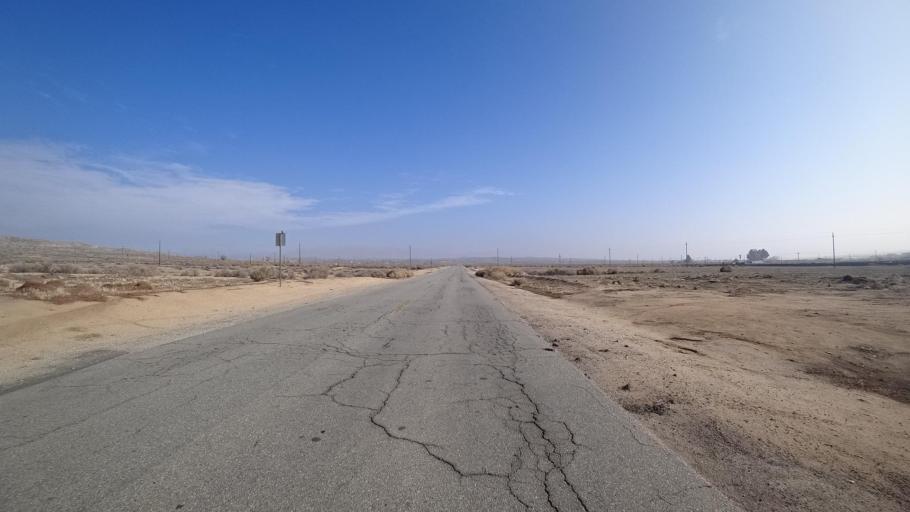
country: US
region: California
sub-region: Kern County
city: Ford City
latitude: 35.1546
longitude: -119.4350
